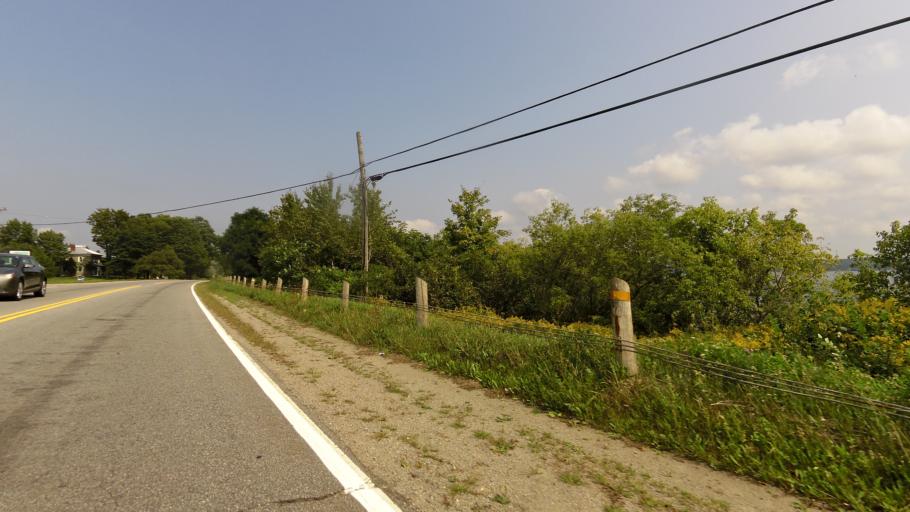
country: CA
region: Ontario
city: Brockville
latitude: 44.6487
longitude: -75.5985
